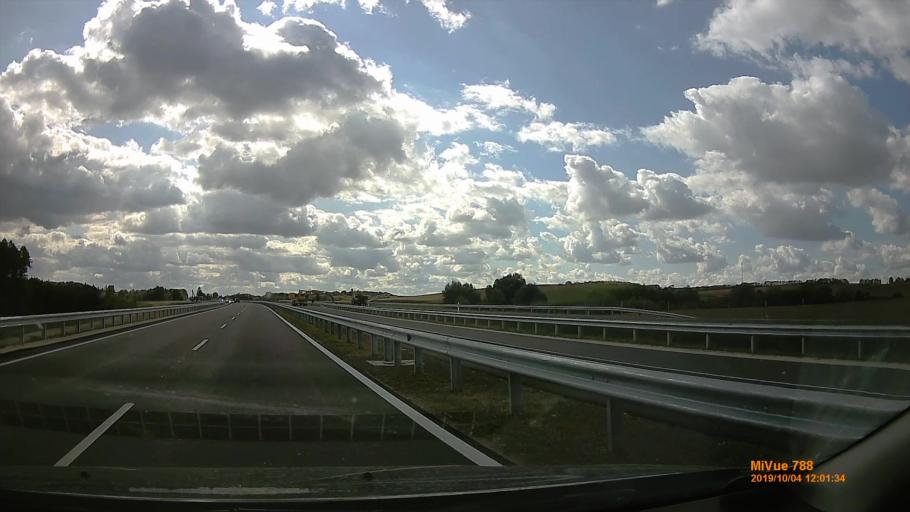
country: HU
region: Somogy
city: Karad
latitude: 46.6109
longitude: 17.7977
